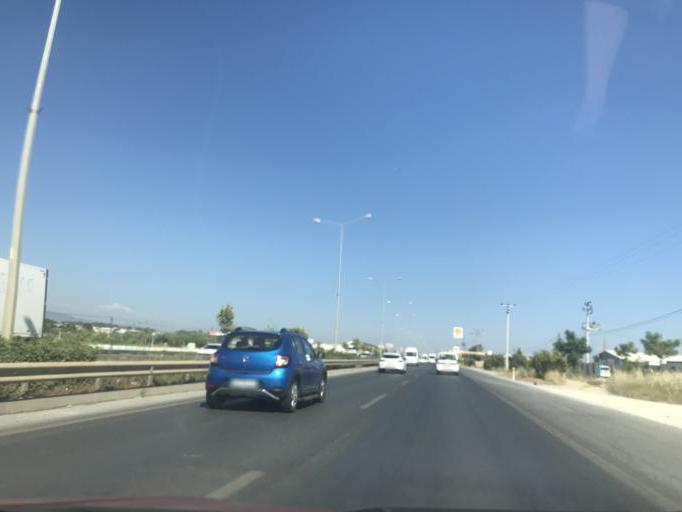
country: TR
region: Antalya
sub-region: Manavgat
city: Side
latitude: 36.8126
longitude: 31.3723
